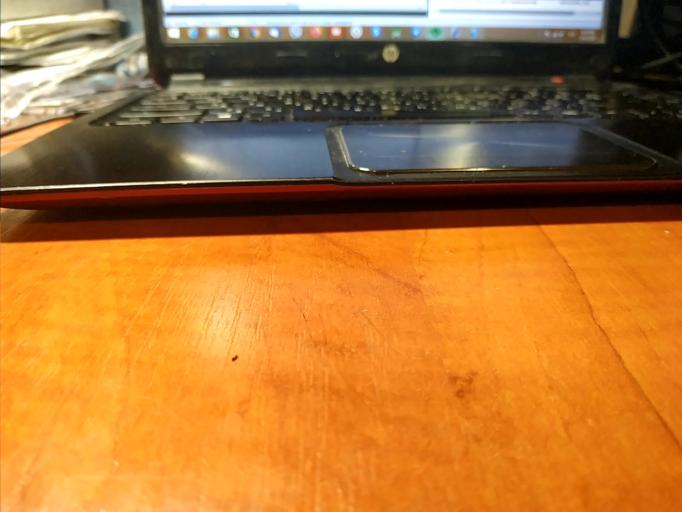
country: RU
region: Arkhangelskaya
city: Onega
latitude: 63.6496
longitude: 36.7289
